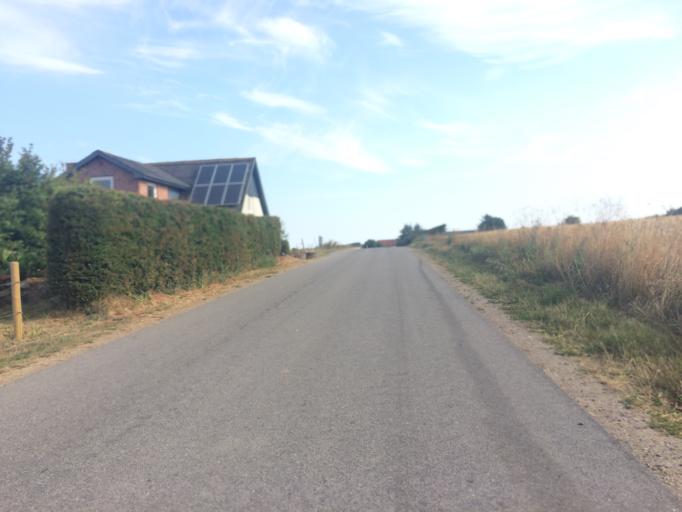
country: DK
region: Central Jutland
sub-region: Holstebro Kommune
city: Vinderup
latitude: 56.5796
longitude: 8.7582
